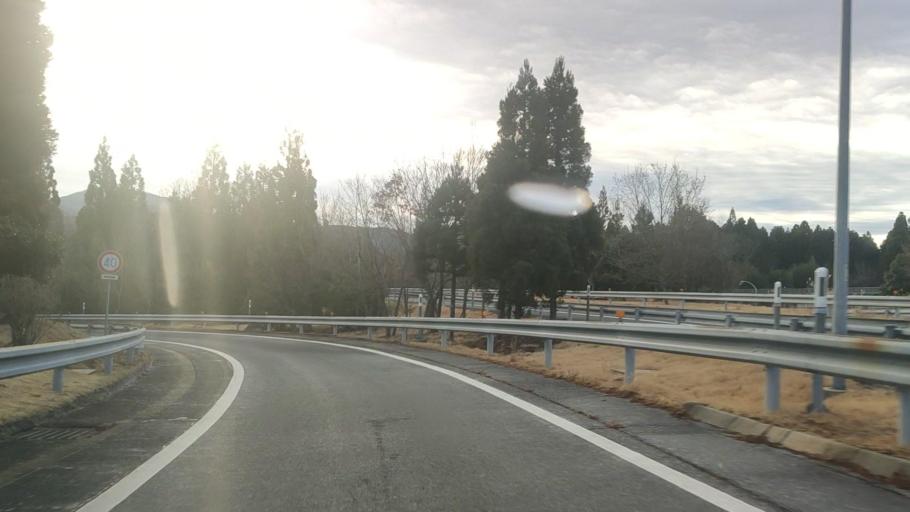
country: JP
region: Oita
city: Beppu
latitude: 33.2585
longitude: 131.3285
